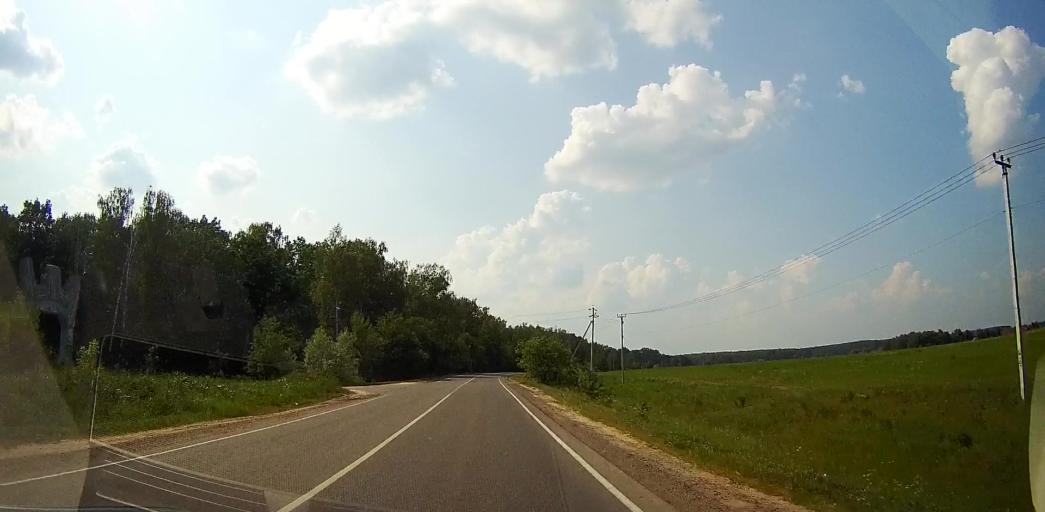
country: RU
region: Moskovskaya
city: Il'inskoye
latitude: 55.1988
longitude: 37.9702
